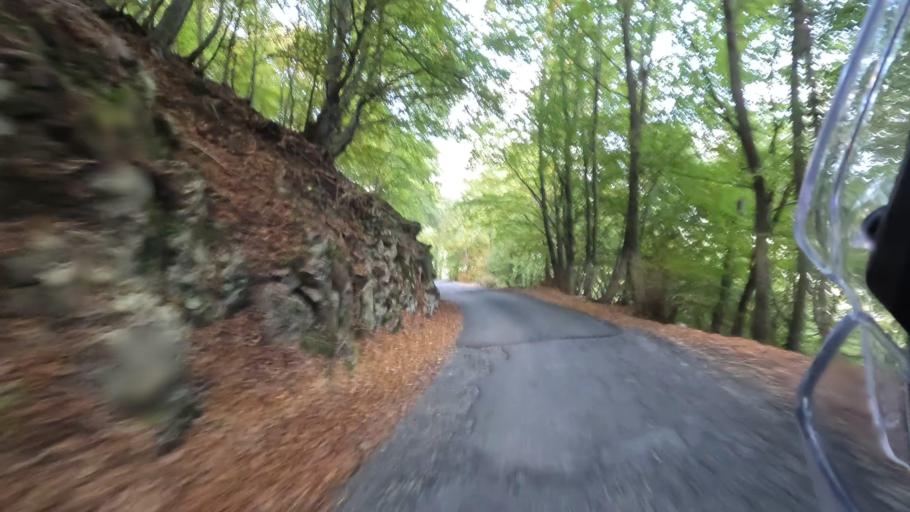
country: IT
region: Lombardy
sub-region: Provincia di Como
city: Pigra
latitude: 45.9654
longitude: 9.1195
